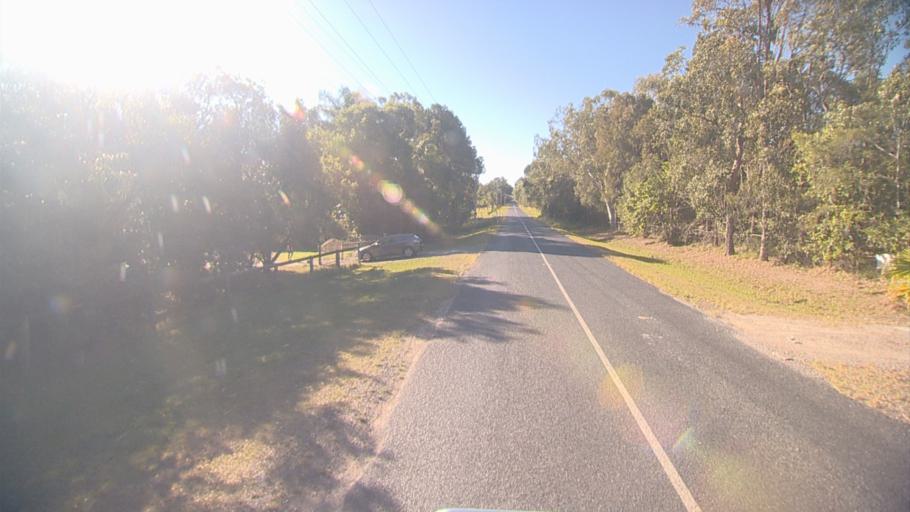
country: AU
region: Queensland
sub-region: Logan
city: Logan Reserve
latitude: -27.7369
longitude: 153.1033
